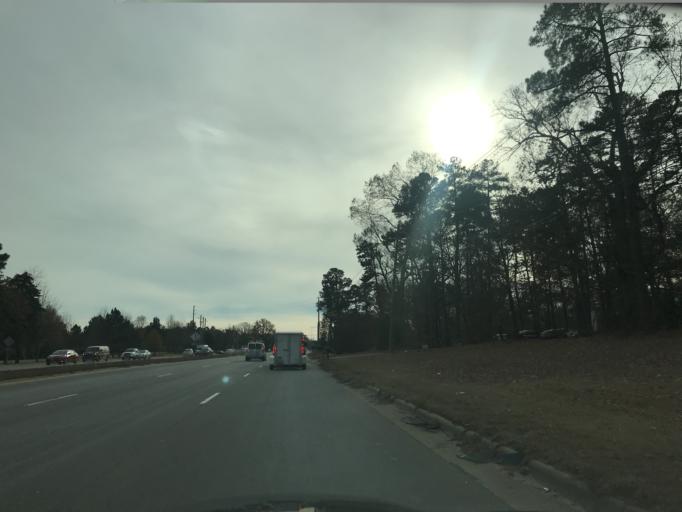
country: US
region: North Carolina
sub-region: Wake County
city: Knightdale
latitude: 35.8675
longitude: -78.5459
